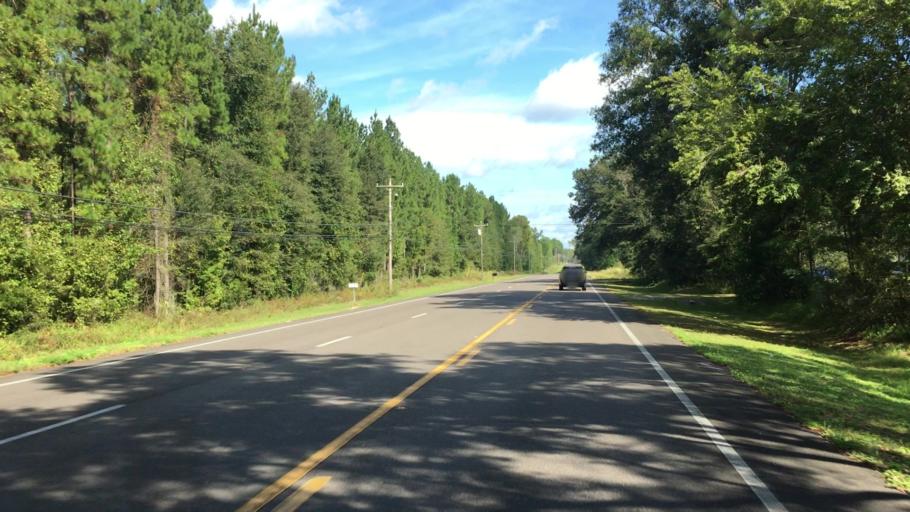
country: US
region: Florida
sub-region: Alachua County
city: Gainesville
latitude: 29.7308
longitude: -82.2768
